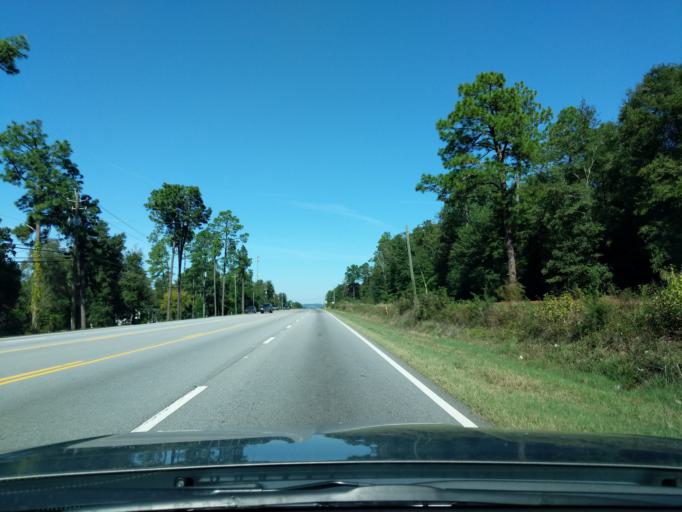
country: US
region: Georgia
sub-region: Richmond County
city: Augusta
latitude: 33.3728
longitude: -81.9988
